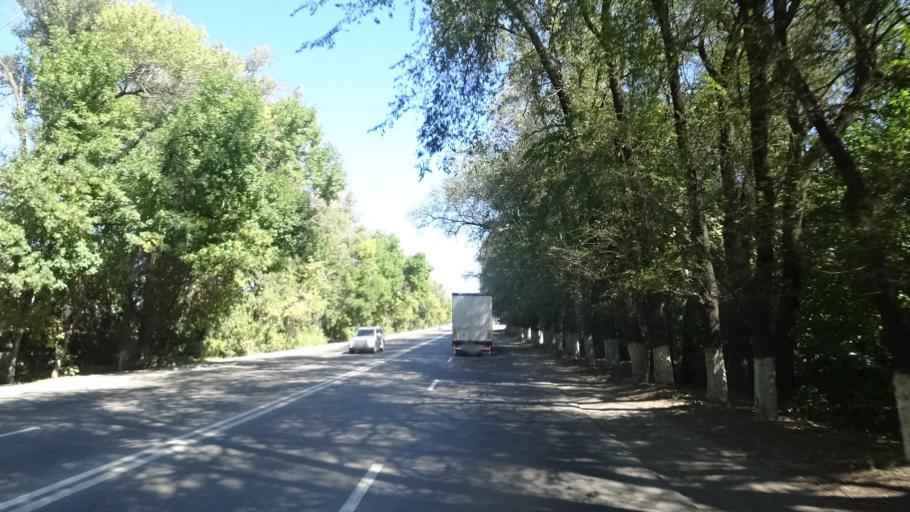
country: KZ
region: Almaty Oblysy
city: Energeticheskiy
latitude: 43.3265
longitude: 77.0315
